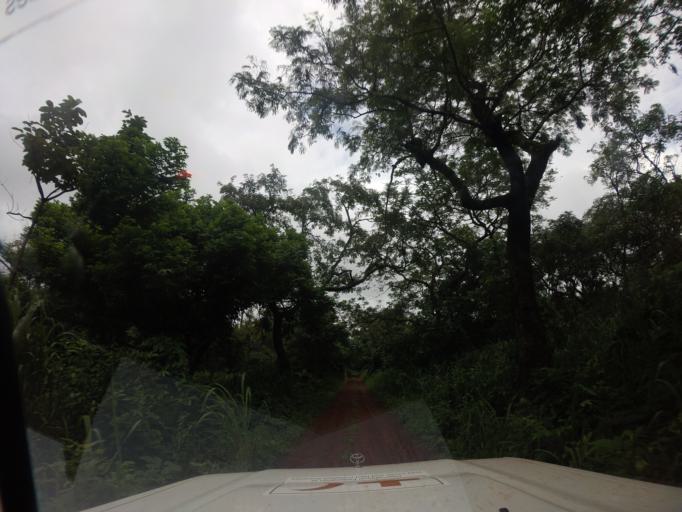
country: SL
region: Northern Province
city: Kamakwie
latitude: 9.6875
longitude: -12.2619
